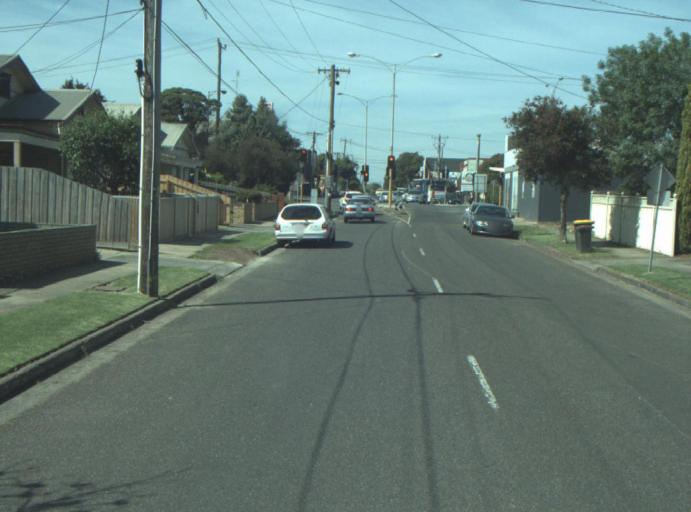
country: AU
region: Victoria
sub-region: Greater Geelong
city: Geelong West
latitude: -38.1312
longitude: 144.3501
